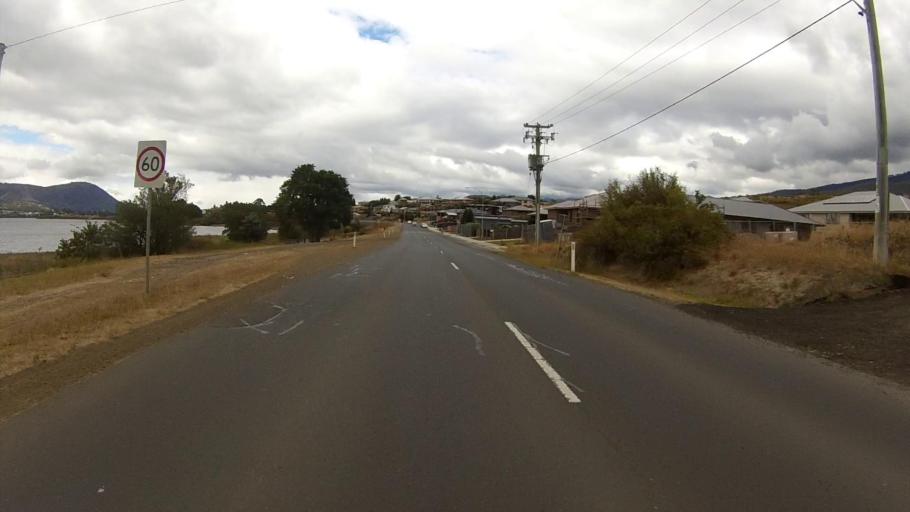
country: AU
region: Tasmania
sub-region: Glenorchy
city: Granton
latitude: -42.7566
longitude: 147.2356
